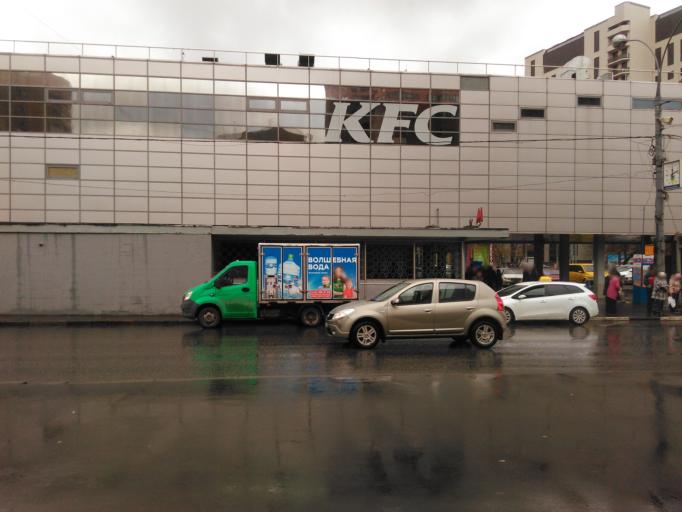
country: RU
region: Moscow
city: Taganskiy
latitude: 55.7318
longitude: 37.6642
